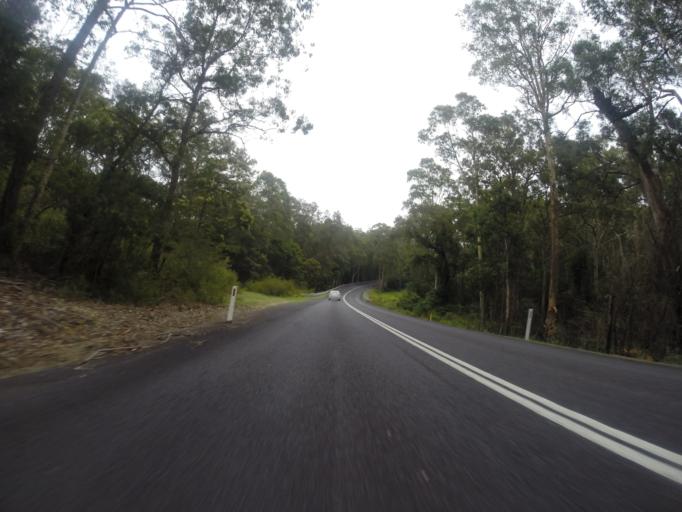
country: AU
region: New South Wales
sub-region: Eurobodalla
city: Batemans Bay
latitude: -35.6568
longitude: 150.2796
